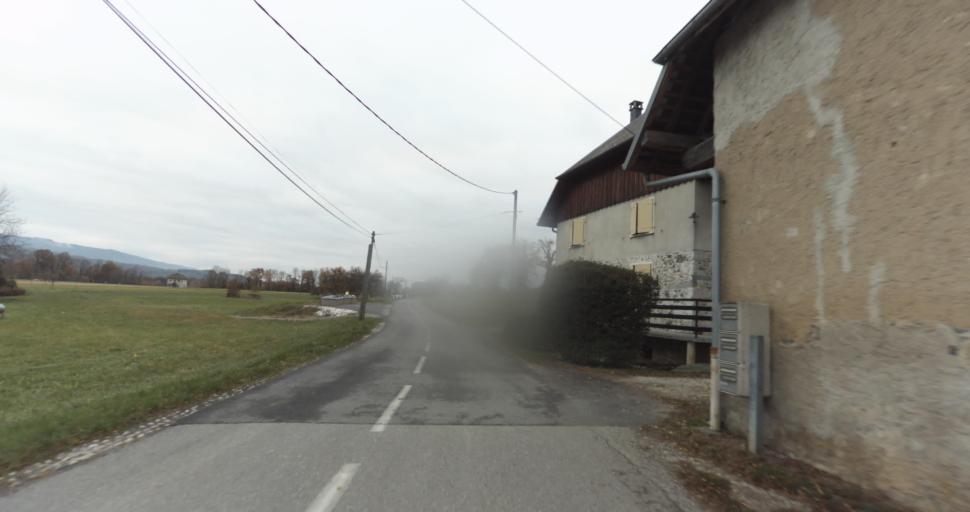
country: FR
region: Rhone-Alpes
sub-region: Departement de la Savoie
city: Albens
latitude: 45.7705
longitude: 5.9638
